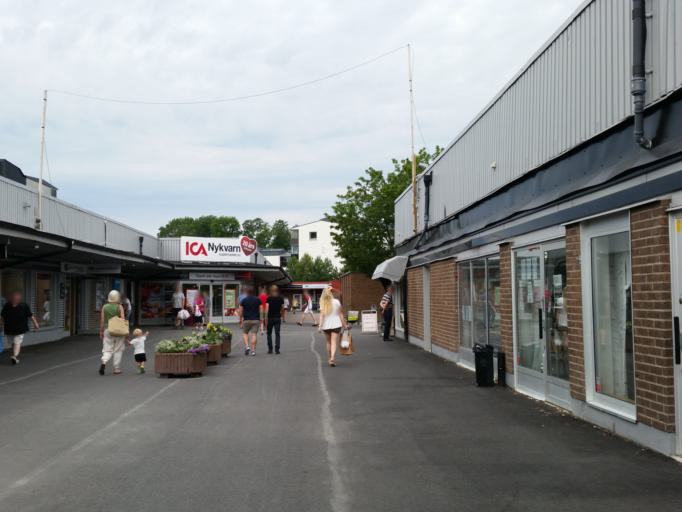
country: SE
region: Stockholm
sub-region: Nykvarns Kommun
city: Nykvarn
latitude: 59.1780
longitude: 17.4308
